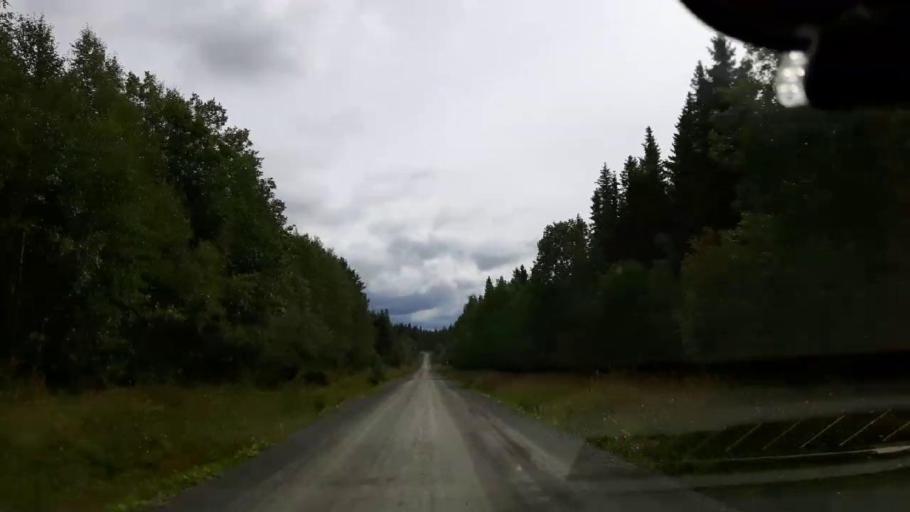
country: SE
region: Jaemtland
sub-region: Krokoms Kommun
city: Valla
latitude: 63.6445
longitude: 13.9908
